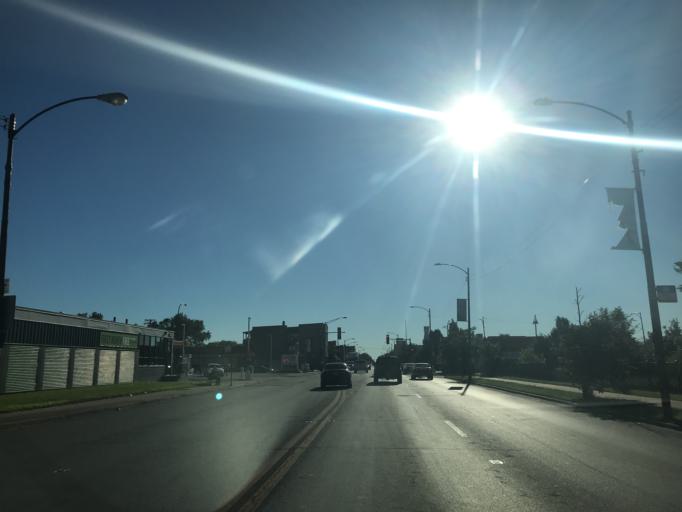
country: US
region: Illinois
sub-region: Cook County
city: Cicero
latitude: 41.8657
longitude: -87.7629
